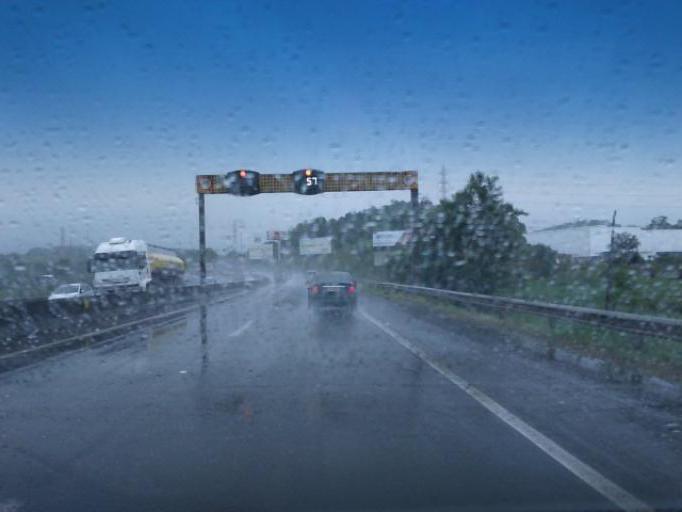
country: BR
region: Santa Catarina
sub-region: Joinville
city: Joinville
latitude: -26.3899
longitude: -48.8400
